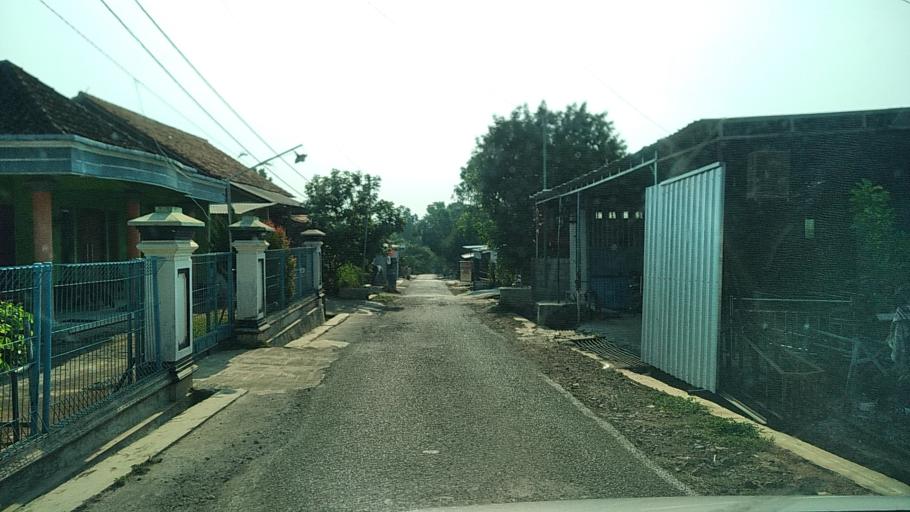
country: ID
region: Central Java
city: Semarang
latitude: -7.0262
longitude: 110.3109
